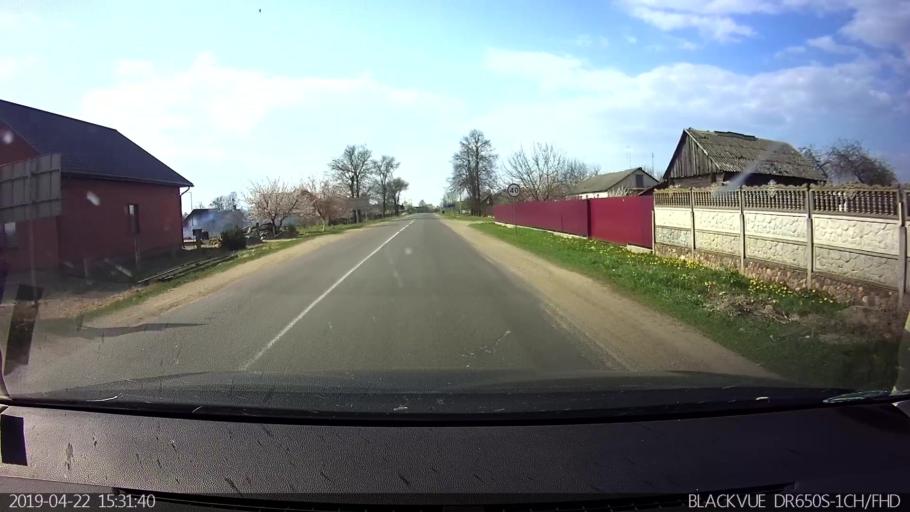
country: BY
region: Brest
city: Vysokaye
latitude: 52.4018
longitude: 23.3861
